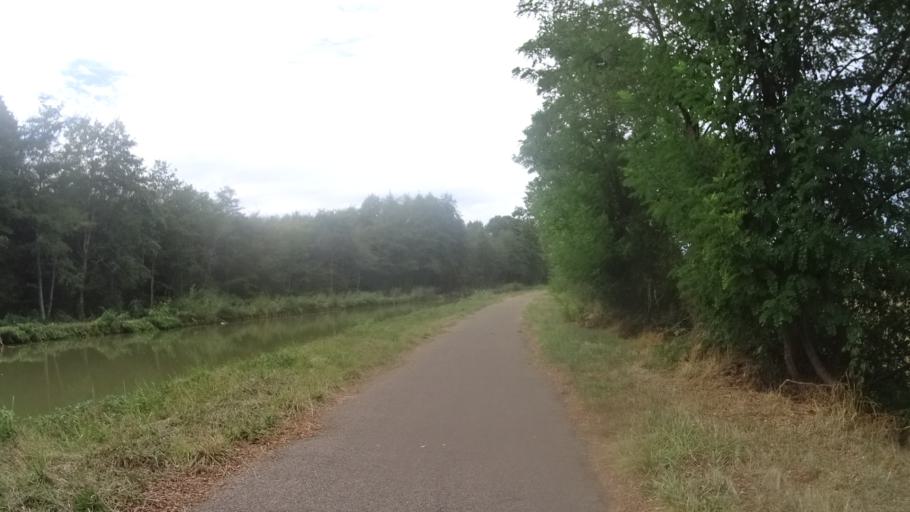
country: FR
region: Bourgogne
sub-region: Departement de la Nievre
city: Imphy
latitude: 46.9280
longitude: 3.2263
